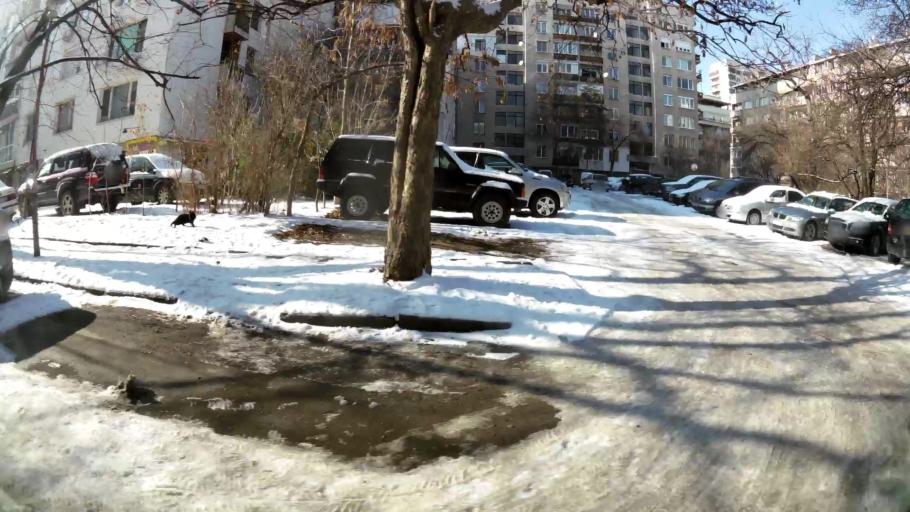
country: BG
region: Sofia-Capital
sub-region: Stolichna Obshtina
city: Sofia
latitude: 42.6772
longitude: 23.3086
